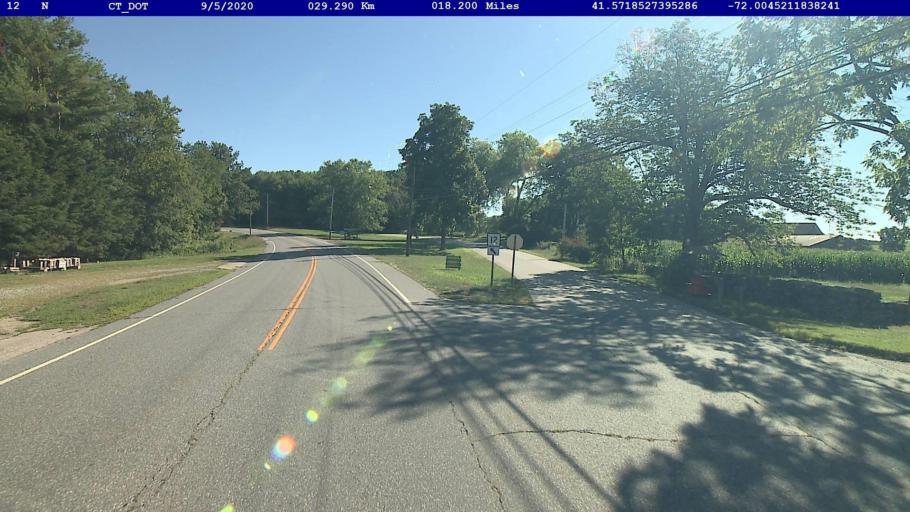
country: US
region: Connecticut
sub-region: New London County
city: Lisbon
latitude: 41.5719
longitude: -72.0046
